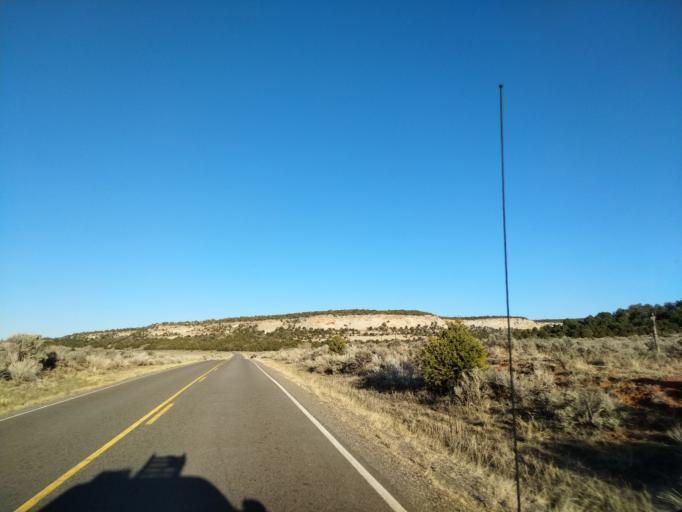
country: US
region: Colorado
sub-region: Mesa County
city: Fruita
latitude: 38.9832
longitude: -108.8034
